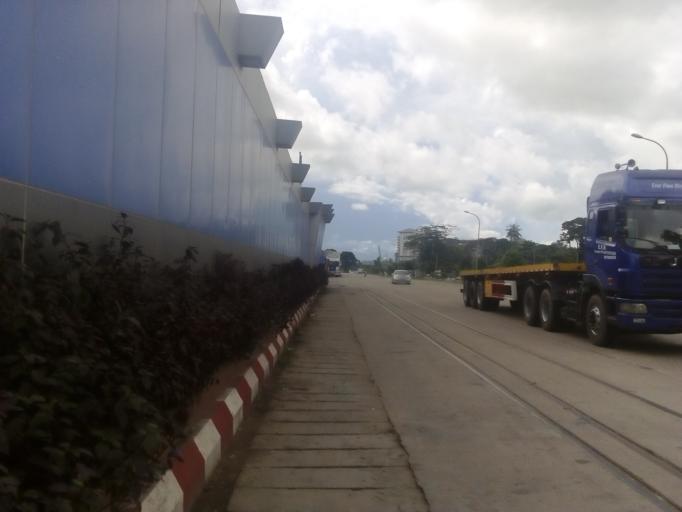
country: MM
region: Yangon
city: Yangon
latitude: 16.7793
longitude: 96.1339
